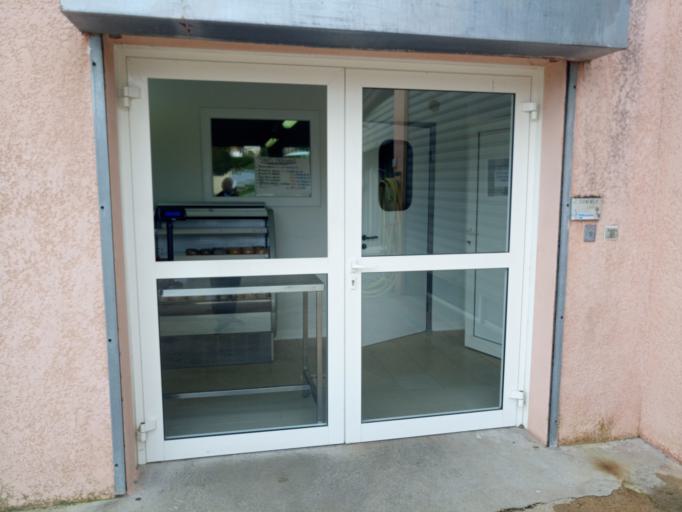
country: FR
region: Corsica
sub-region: Departement de la Corse-du-Sud
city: Afa
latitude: 41.9702
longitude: 8.7754
